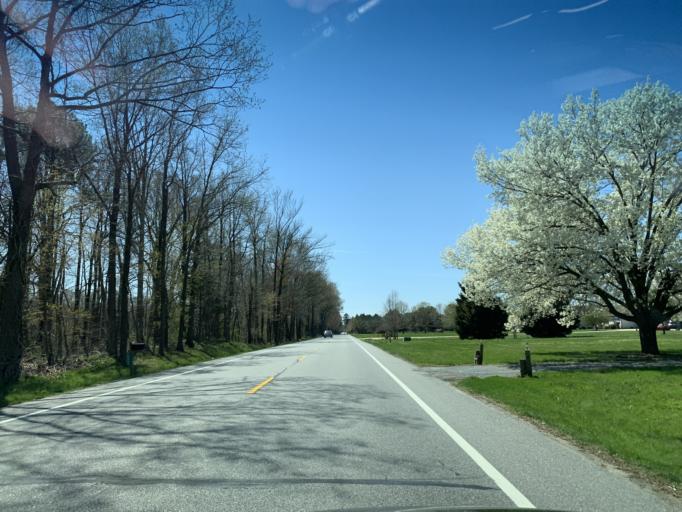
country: US
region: Maryland
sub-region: Talbot County
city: Easton
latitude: 38.8363
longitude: -76.0287
